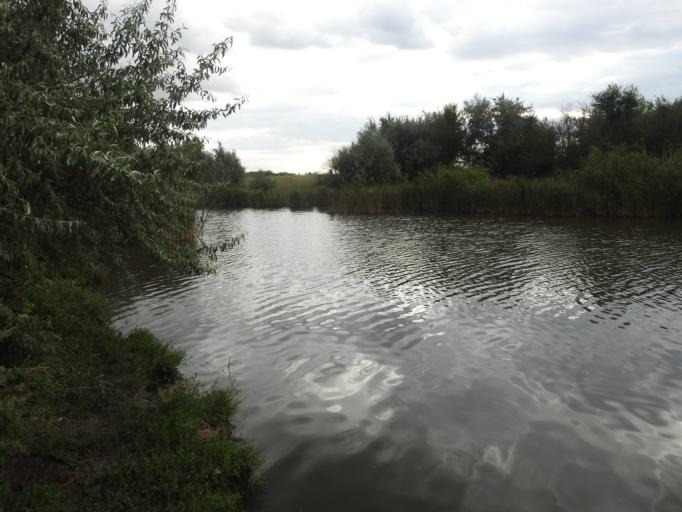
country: RU
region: Saratov
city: Shumeyka
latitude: 51.4120
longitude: 46.2936
